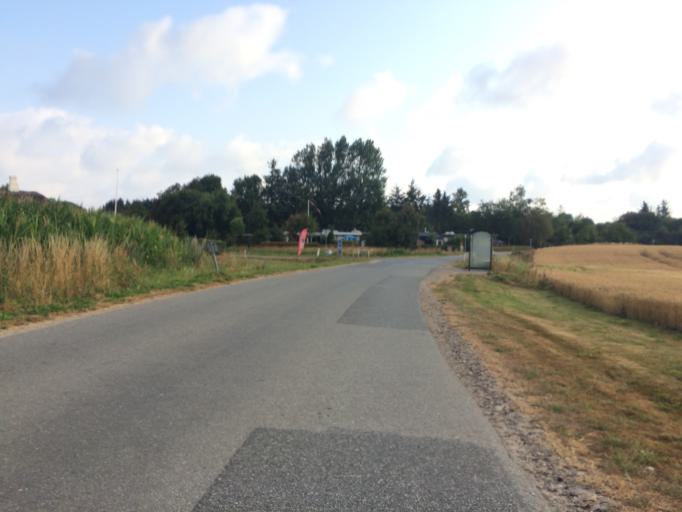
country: DK
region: Central Jutland
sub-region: Holstebro Kommune
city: Vinderup
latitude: 56.6178
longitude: 8.7341
